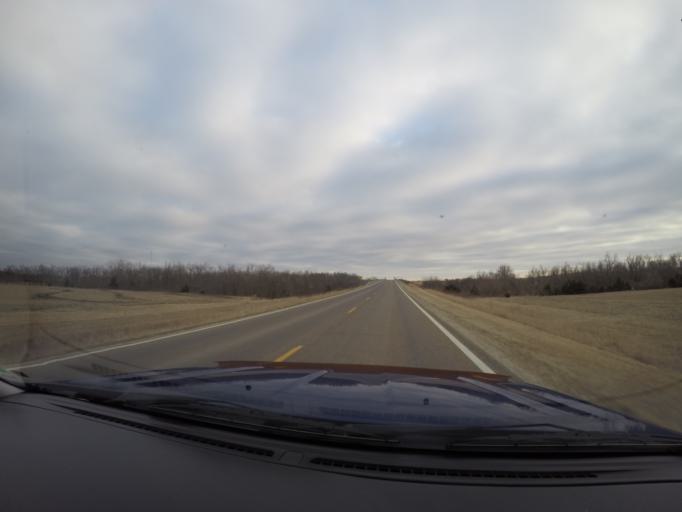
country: US
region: Kansas
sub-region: Morris County
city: Council Grove
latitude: 38.8600
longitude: -96.5043
